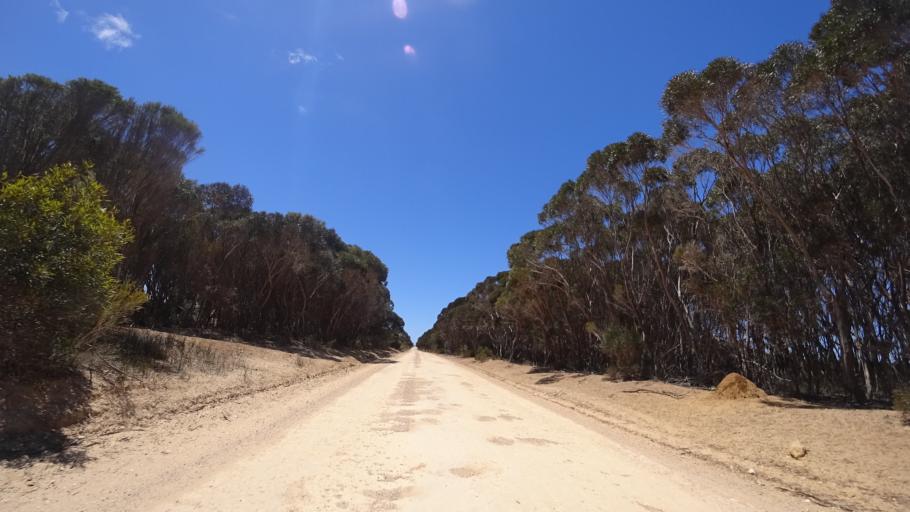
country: AU
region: South Australia
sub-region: Yankalilla
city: Normanville
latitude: -35.8323
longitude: 138.0942
